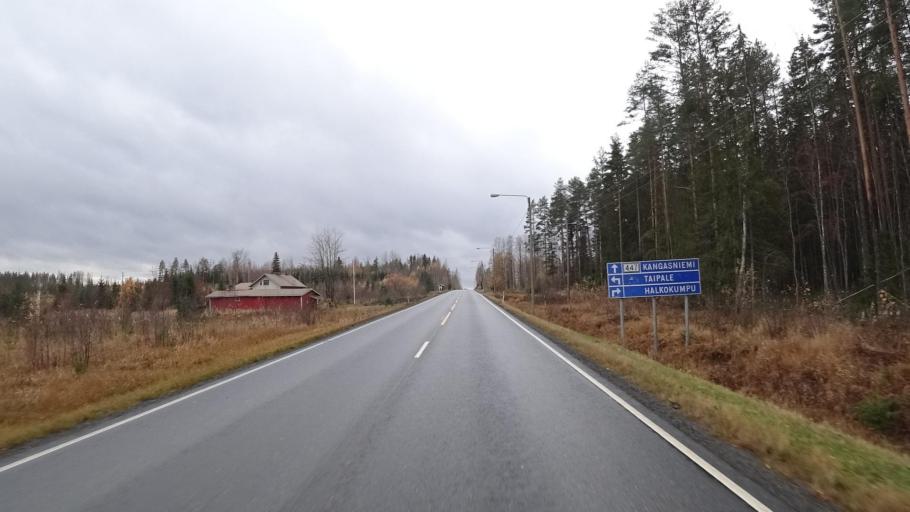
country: FI
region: Southern Savonia
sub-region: Mikkeli
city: Kangasniemi
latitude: 62.1751
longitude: 26.8630
